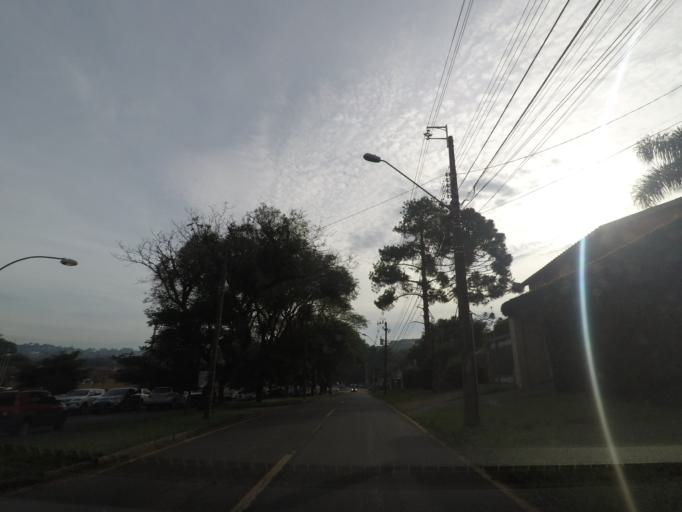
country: BR
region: Parana
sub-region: Curitiba
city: Curitiba
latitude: -25.4240
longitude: -49.3058
